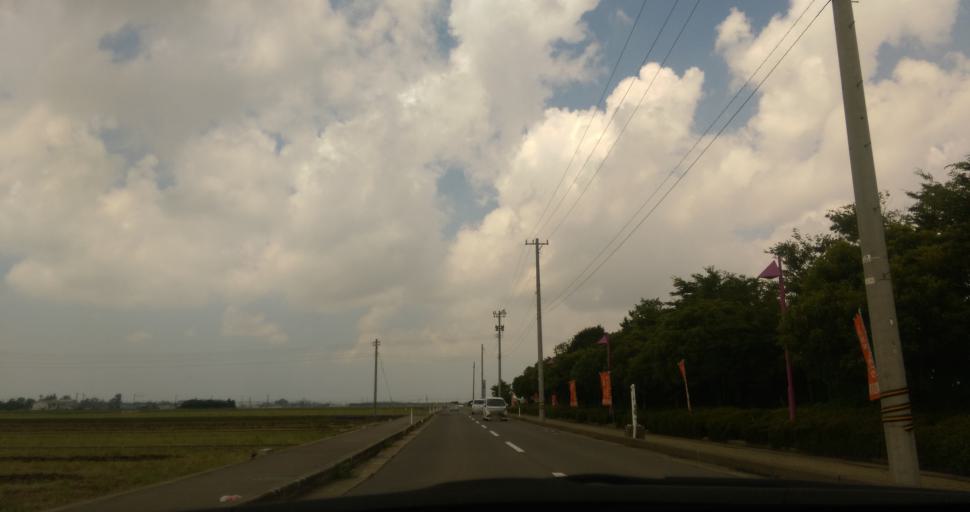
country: JP
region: Fukui
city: Mikuni
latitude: 36.1485
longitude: 136.1873
